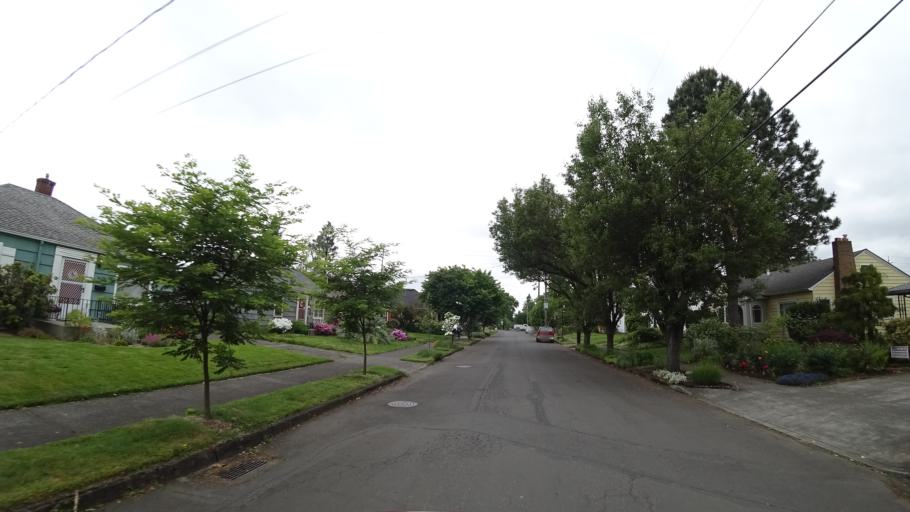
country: US
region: Oregon
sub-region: Multnomah County
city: Lents
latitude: 45.4894
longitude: -122.6149
